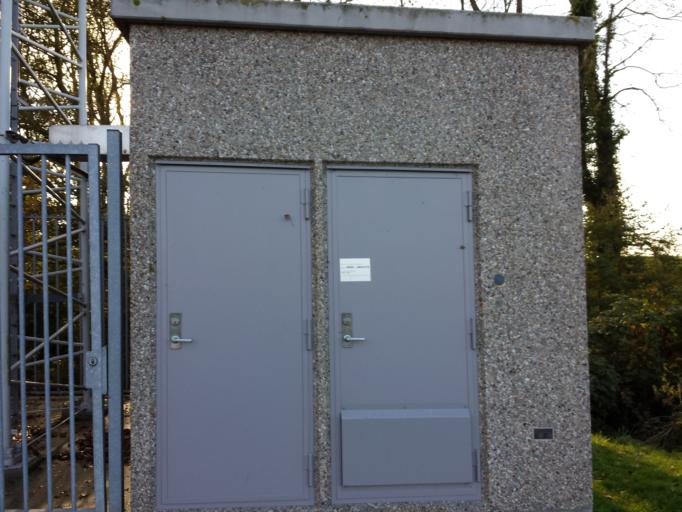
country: NL
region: Zeeland
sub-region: Gemeente Vlissingen
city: Vlissingen
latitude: 51.4013
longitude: 3.5461
